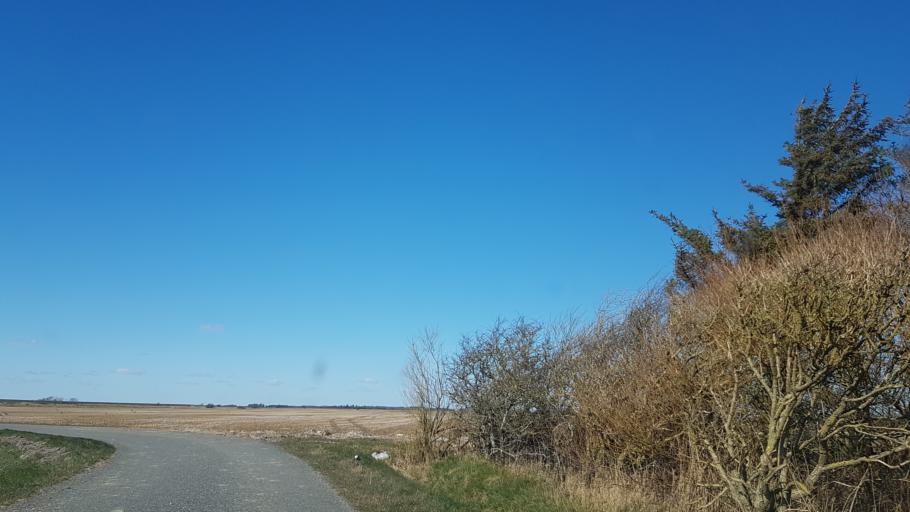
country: DK
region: South Denmark
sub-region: Esbjerg Kommune
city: Ribe
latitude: 55.2592
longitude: 8.6732
